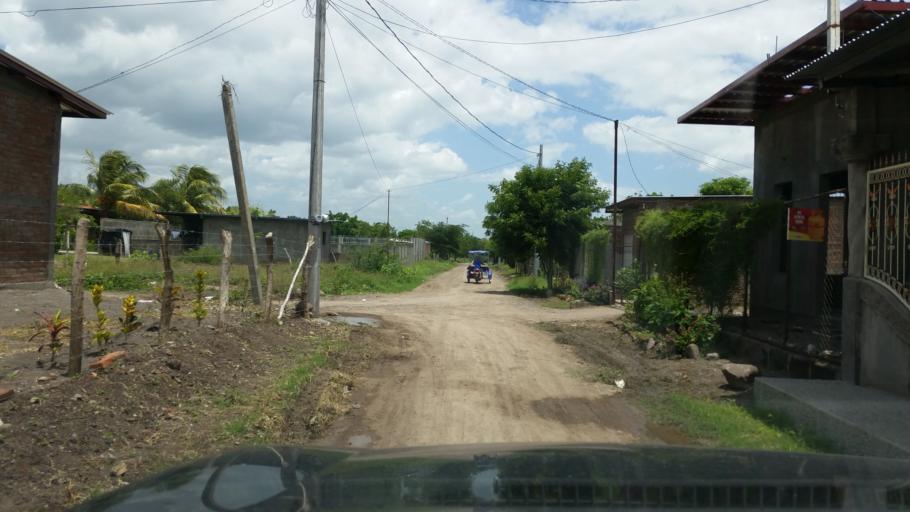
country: NI
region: Matagalpa
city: Ciudad Dario
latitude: 12.8651
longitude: -86.0911
